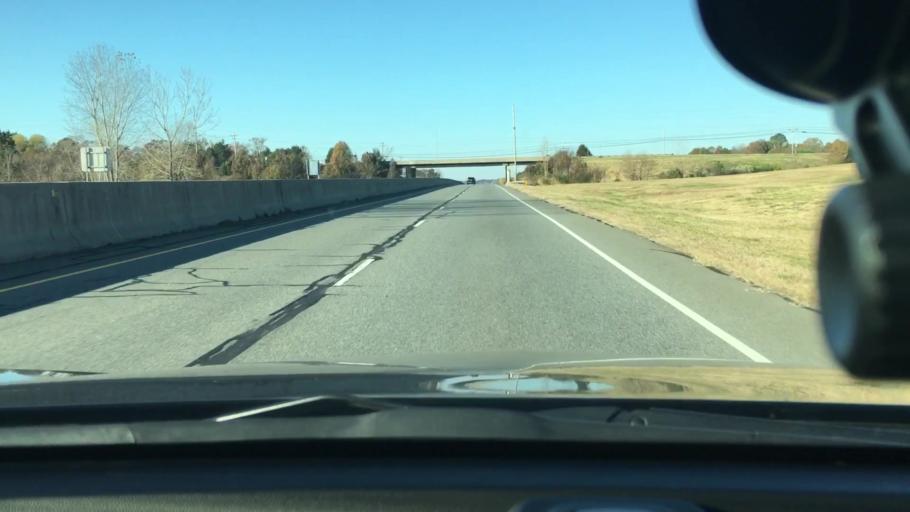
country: US
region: North Carolina
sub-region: Cabarrus County
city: Concord
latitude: 35.3739
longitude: -80.5485
